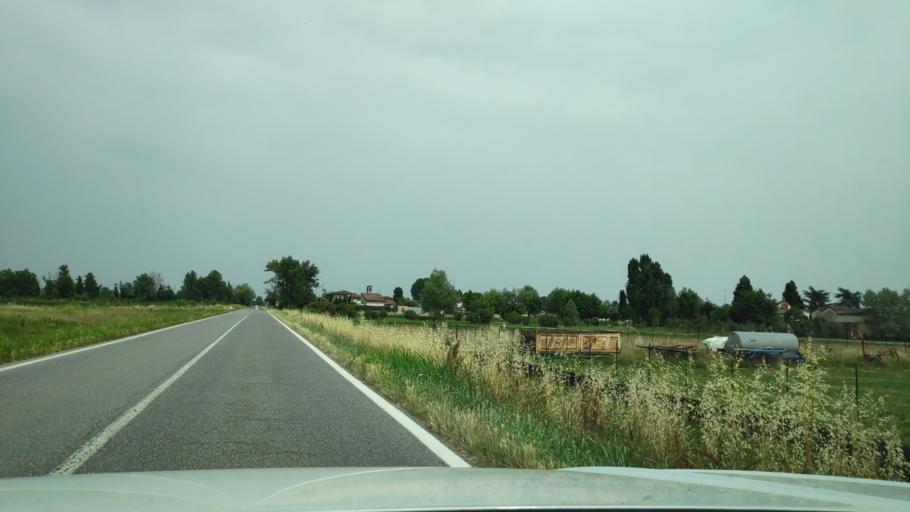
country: IT
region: Lombardy
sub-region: Provincia di Cremona
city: Casaletto di Sopra
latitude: 45.4140
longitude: 9.7979
